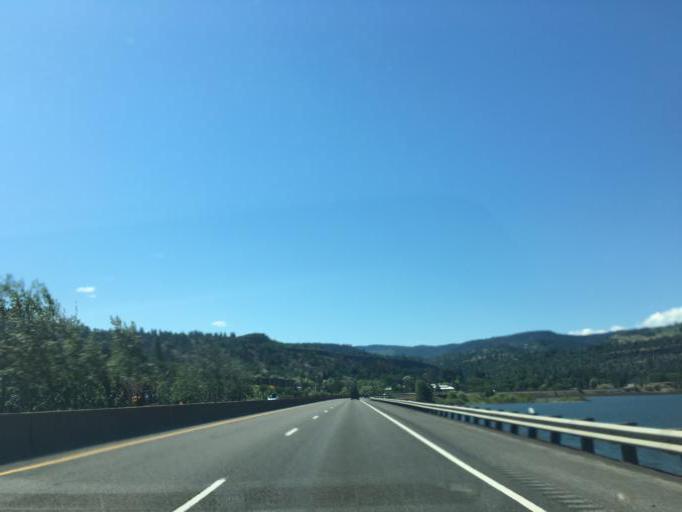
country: US
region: Washington
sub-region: Klickitat County
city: White Salmon
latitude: 45.6886
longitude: -121.3900
